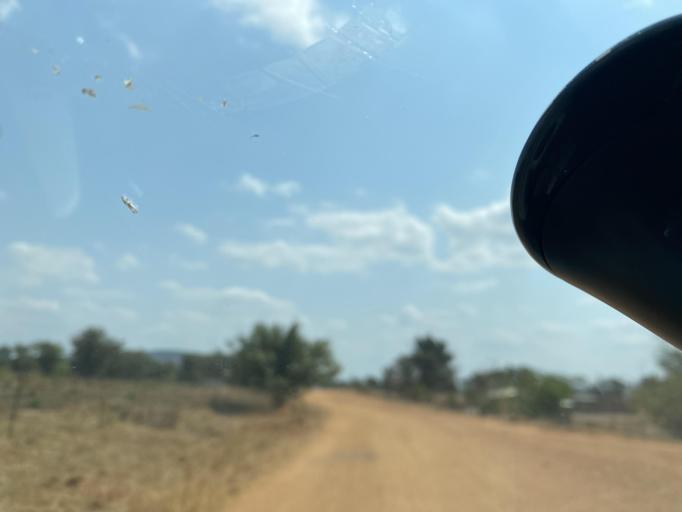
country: ZM
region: Lusaka
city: Chongwe
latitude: -15.5887
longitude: 28.7614
